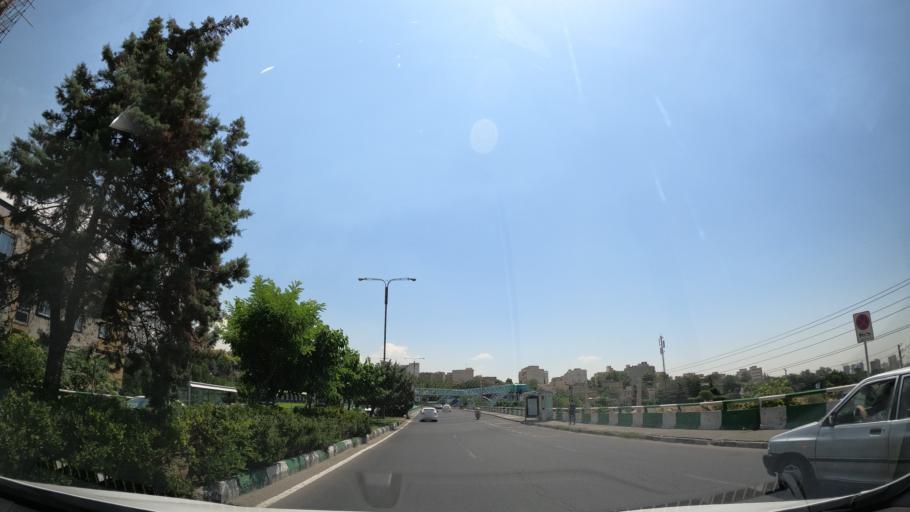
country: IR
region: Tehran
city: Tajrish
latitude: 35.7708
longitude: 51.3854
